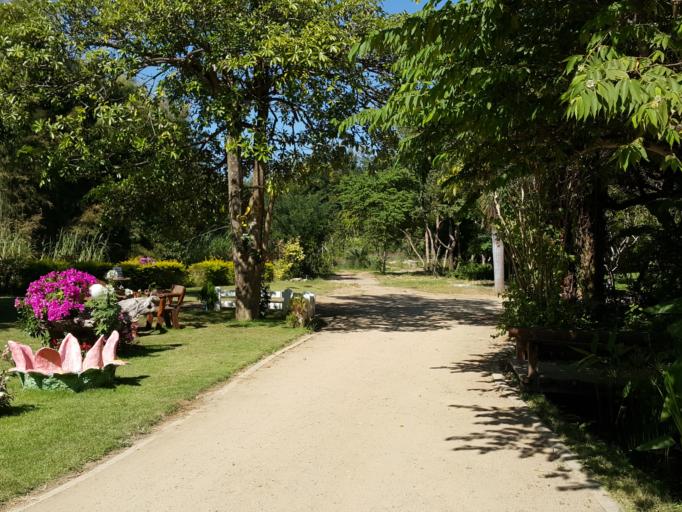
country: TH
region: Mae Hong Son
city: Mae Hi
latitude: 19.3156
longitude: 98.4582
